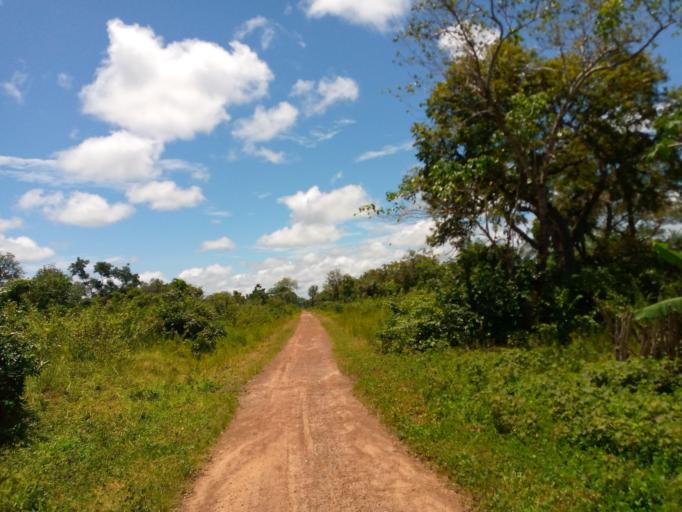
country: SL
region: Northern Province
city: Binkolo
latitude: 9.0713
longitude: -12.1469
